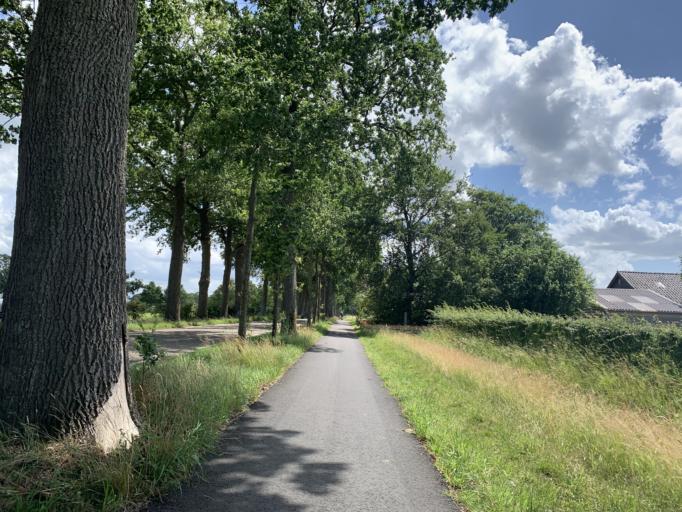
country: NL
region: Drenthe
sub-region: Gemeente Tynaarlo
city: Zuidlaren
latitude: 53.1294
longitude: 6.6601
